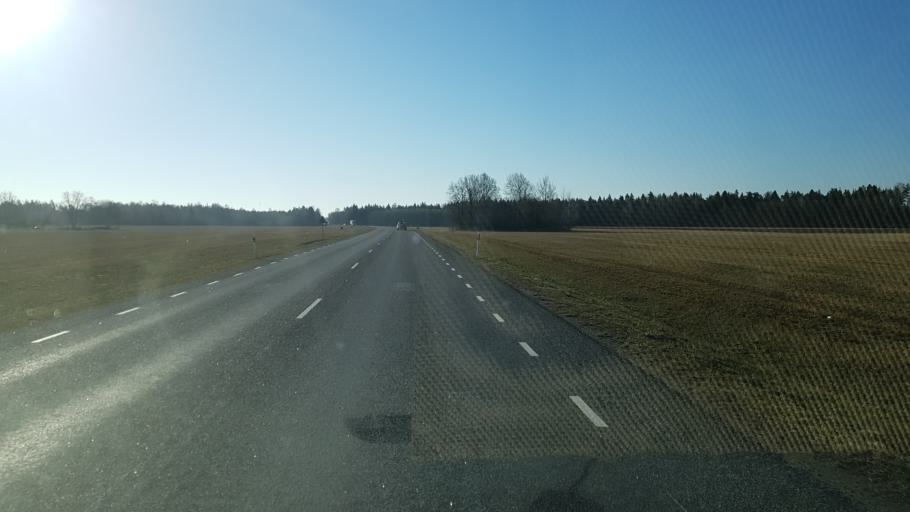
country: EE
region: Jaervamaa
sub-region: Tueri vald
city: Sarevere
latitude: 58.7702
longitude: 25.5224
